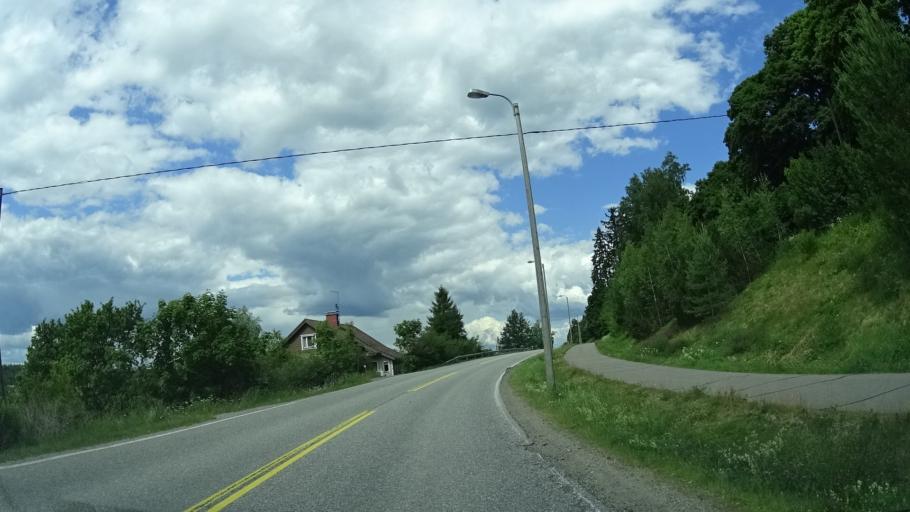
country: FI
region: Uusimaa
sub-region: Helsinki
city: Nurmijaervi
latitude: 60.3848
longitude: 24.6484
